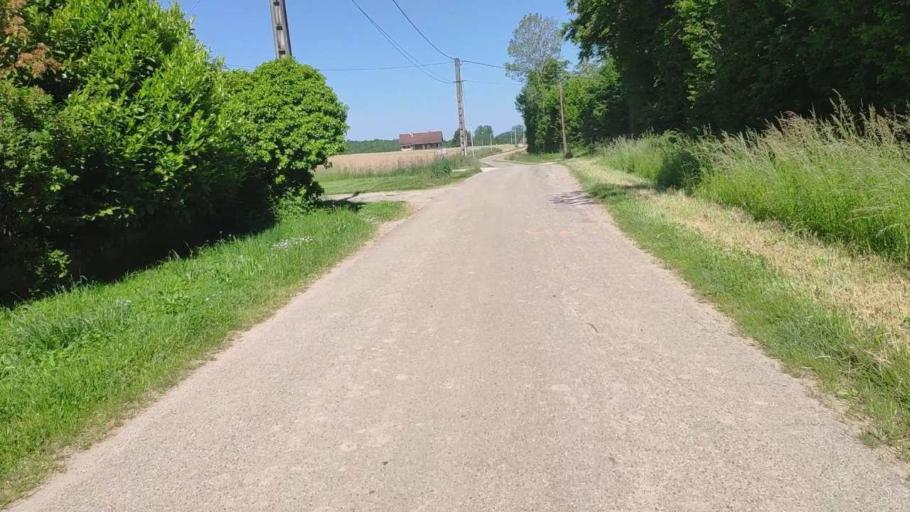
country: FR
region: Franche-Comte
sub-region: Departement du Jura
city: Bletterans
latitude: 46.7895
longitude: 5.4392
